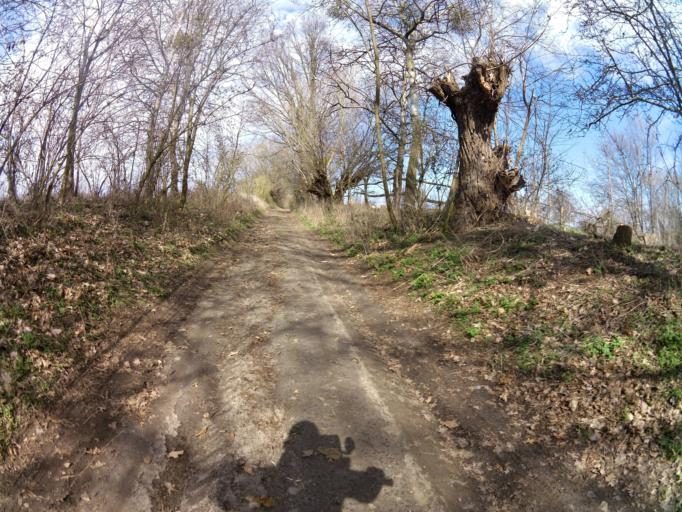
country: PL
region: West Pomeranian Voivodeship
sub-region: Powiat mysliborski
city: Mysliborz
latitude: 52.9729
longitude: 14.8805
